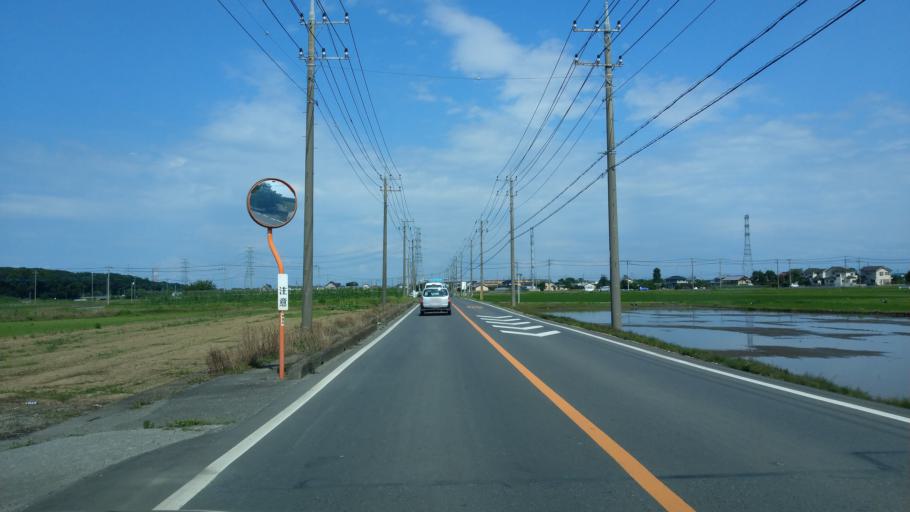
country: JP
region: Saitama
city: Kodamacho-kodamaminami
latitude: 36.2057
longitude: 139.1637
